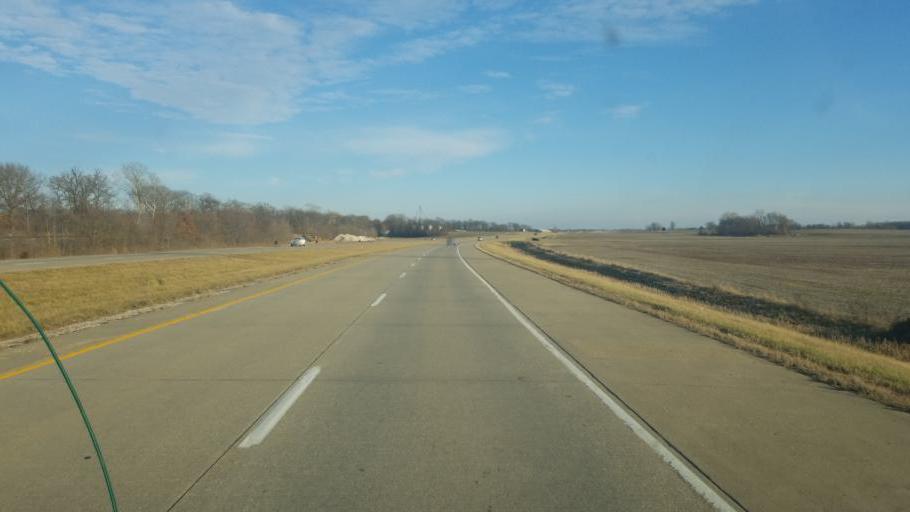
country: US
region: Indiana
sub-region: Knox County
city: Bicknell
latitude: 38.6676
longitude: -87.3320
